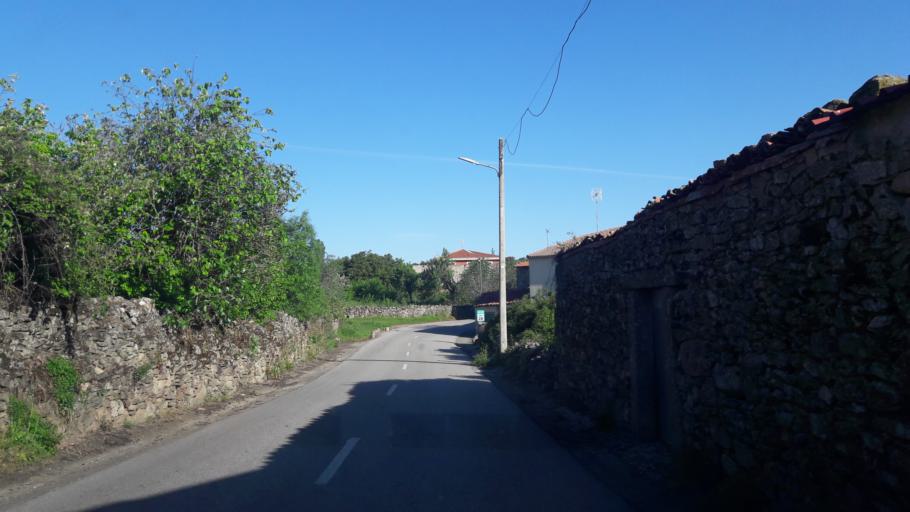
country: ES
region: Castille and Leon
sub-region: Provincia de Salamanca
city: Bogajo
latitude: 40.9056
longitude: -6.5317
